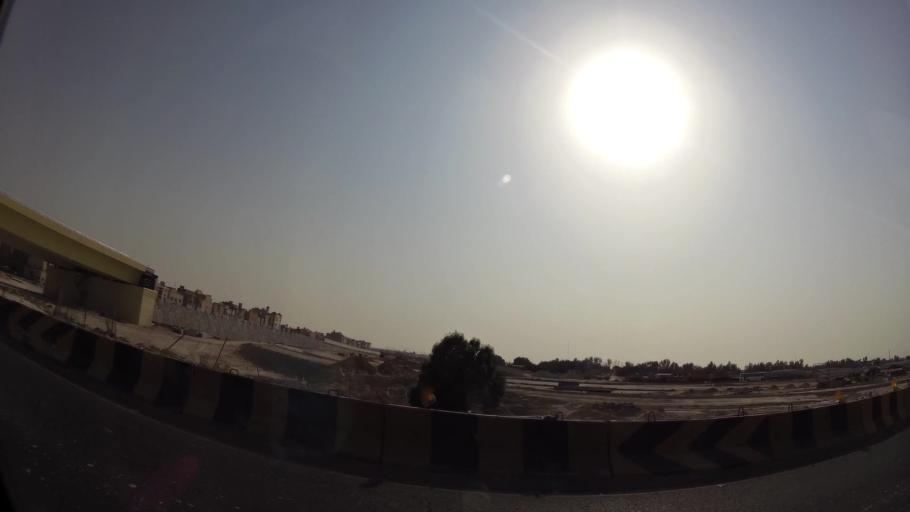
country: KW
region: Muhafazat al Jahra'
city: Al Jahra'
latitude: 29.3301
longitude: 47.7364
